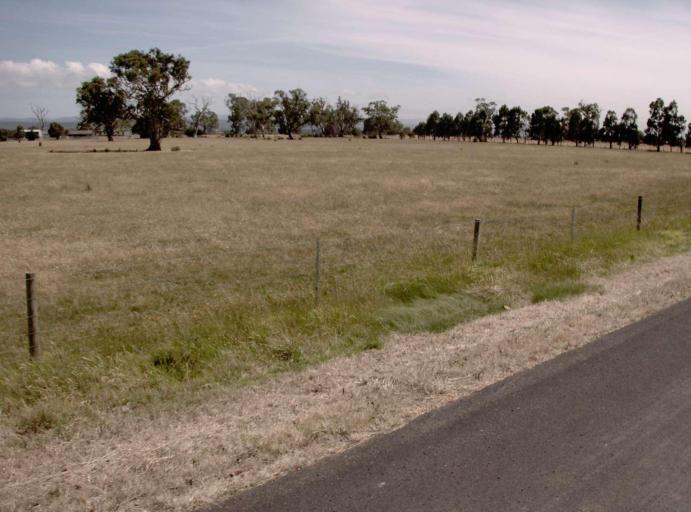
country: AU
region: Victoria
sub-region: Wellington
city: Heyfield
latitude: -38.1360
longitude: 146.7996
